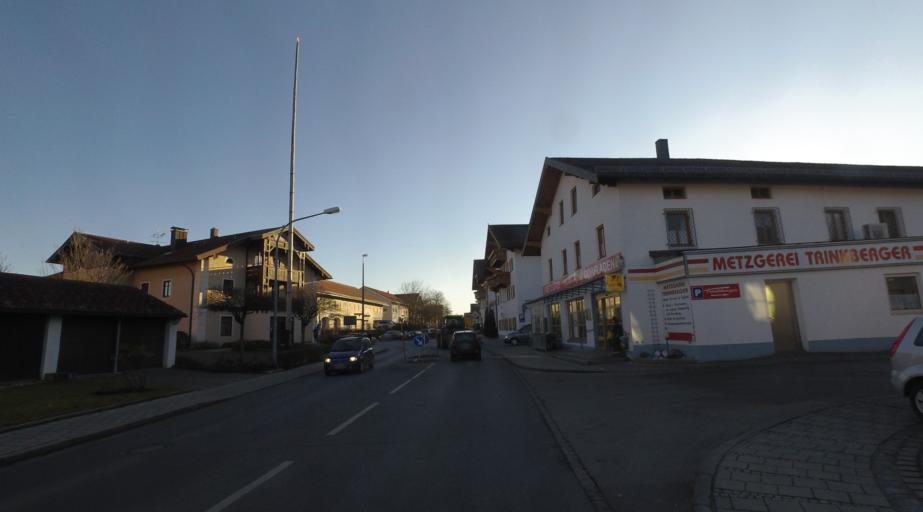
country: DE
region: Bavaria
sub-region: Upper Bavaria
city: Palling
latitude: 48.0014
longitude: 12.6369
